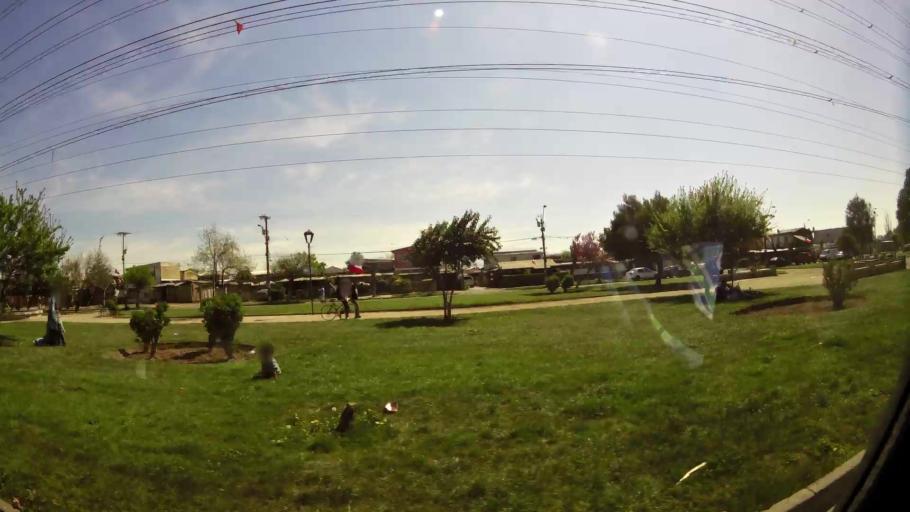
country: CL
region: Santiago Metropolitan
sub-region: Provincia de Santiago
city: Lo Prado
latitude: -33.4968
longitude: -70.7317
